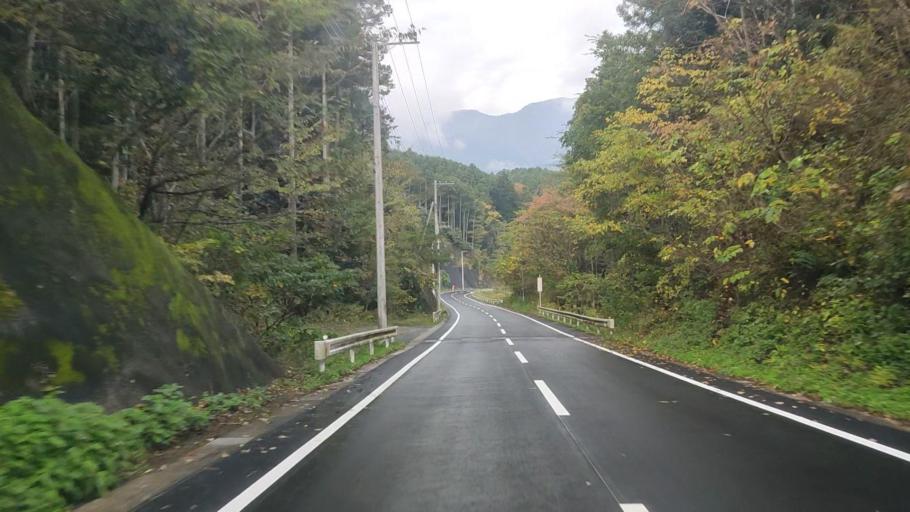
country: JP
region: Shizuoka
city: Fujinomiya
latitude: 35.2736
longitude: 138.4606
